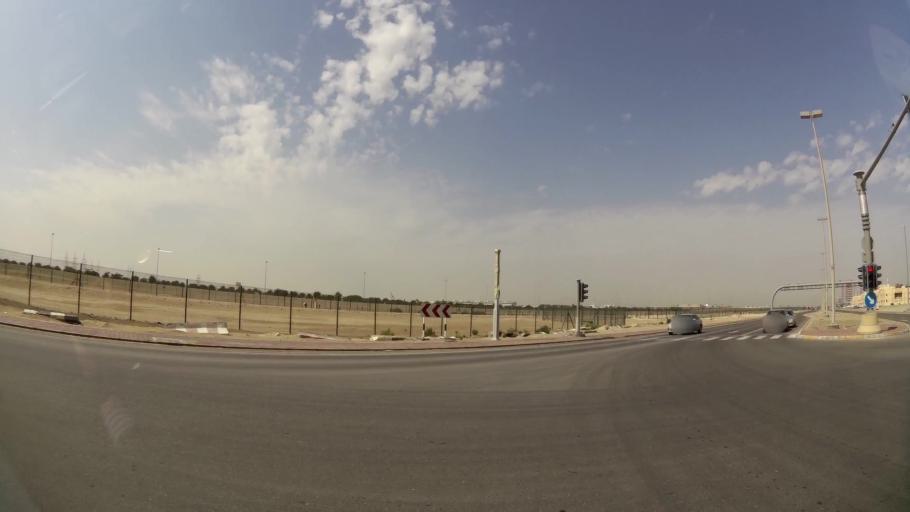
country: AE
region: Abu Dhabi
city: Abu Dhabi
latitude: 24.3149
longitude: 54.5304
